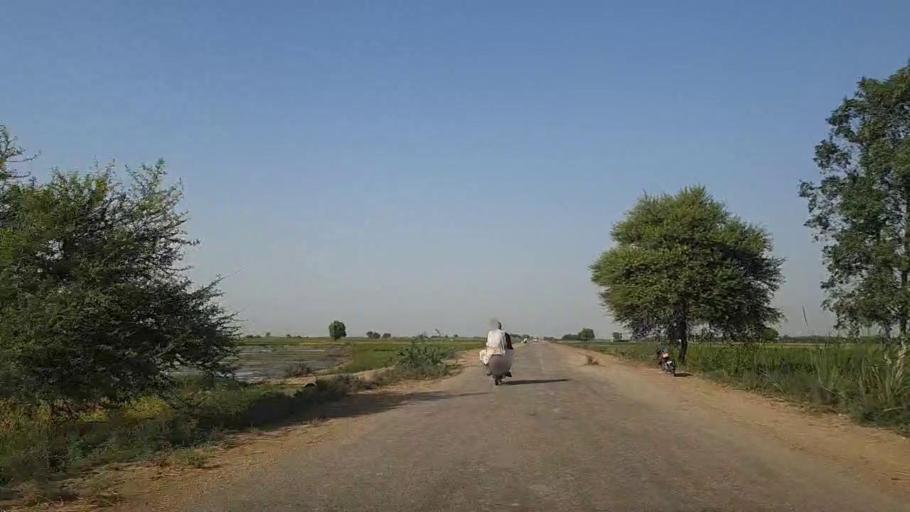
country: PK
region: Sindh
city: Mirpur Batoro
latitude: 24.5872
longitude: 68.3974
